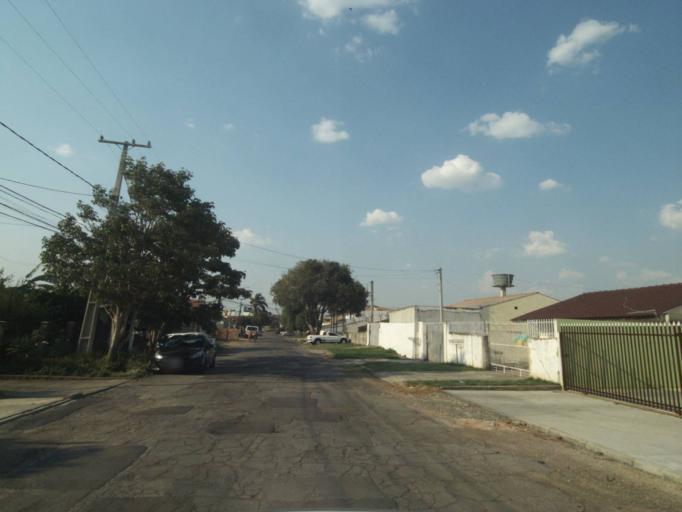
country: BR
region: Parana
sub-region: Sao Jose Dos Pinhais
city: Sao Jose dos Pinhais
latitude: -25.5301
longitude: -49.2373
